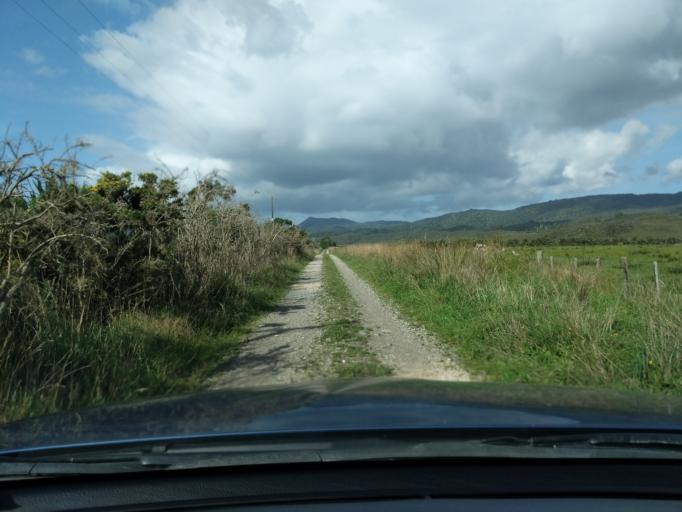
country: NZ
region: Tasman
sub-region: Tasman District
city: Takaka
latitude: -40.6517
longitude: 172.4729
